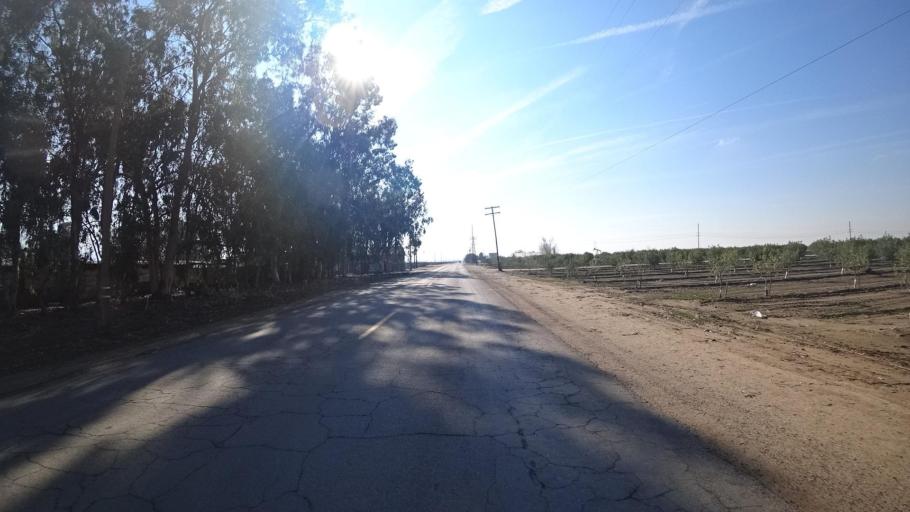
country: US
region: California
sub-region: Kern County
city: Arvin
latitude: 35.2250
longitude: -118.8603
